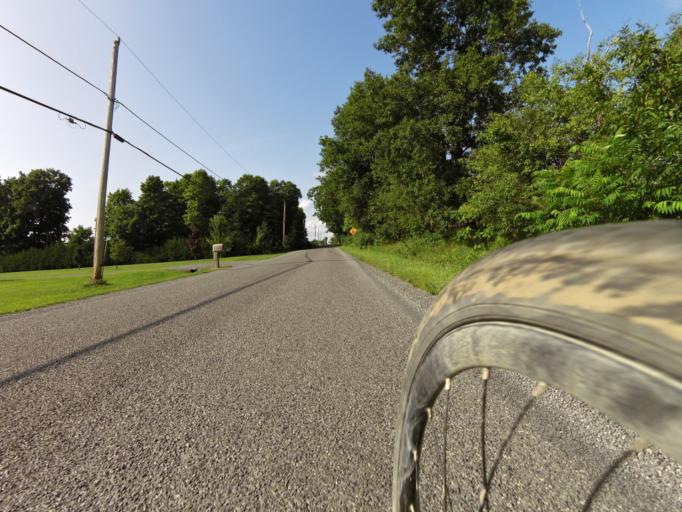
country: CA
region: Ontario
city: Kingston
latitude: 44.3793
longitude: -76.5954
